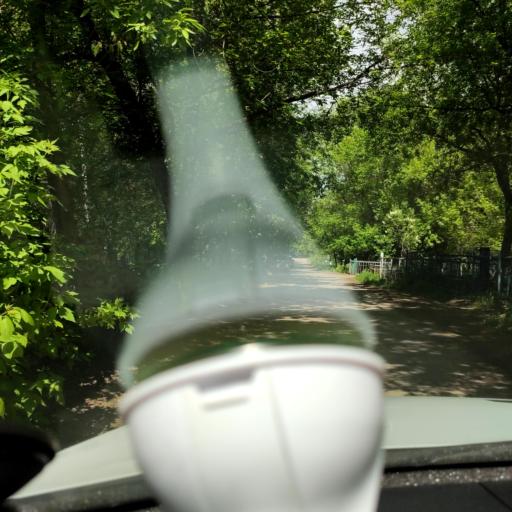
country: RU
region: Samara
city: Petra-Dubrava
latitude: 53.2760
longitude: 50.3204
